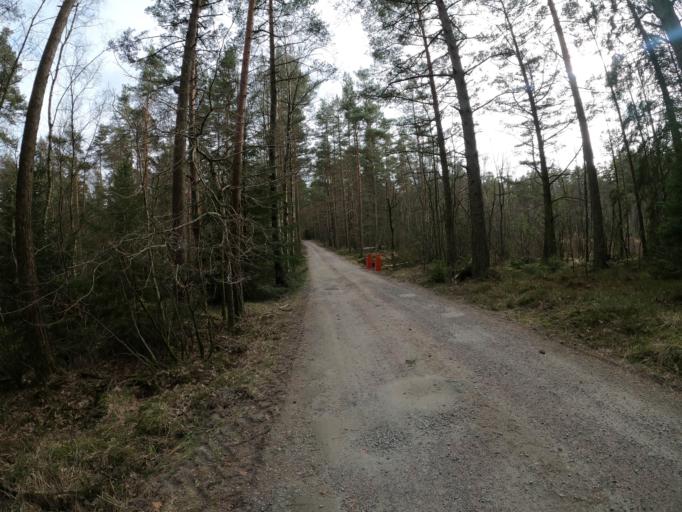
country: SE
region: Vaestra Goetaland
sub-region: Molndal
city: Kallered
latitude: 57.6242
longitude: 12.0755
